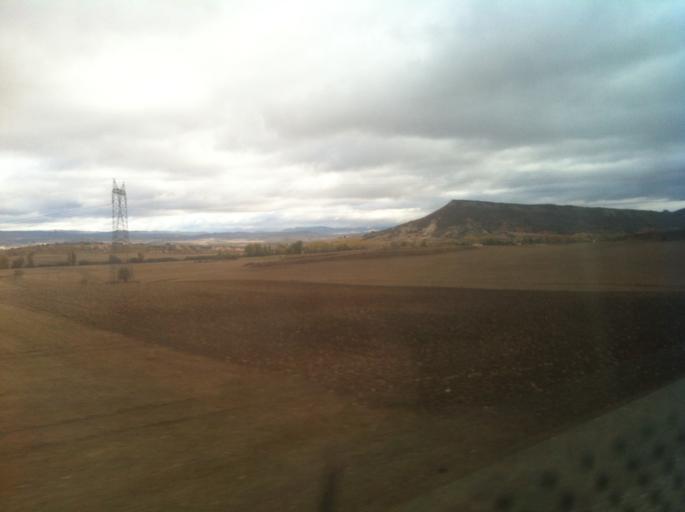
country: ES
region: Castille and Leon
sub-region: Provincia de Burgos
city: Bugedo
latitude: 42.6493
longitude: -3.0370
